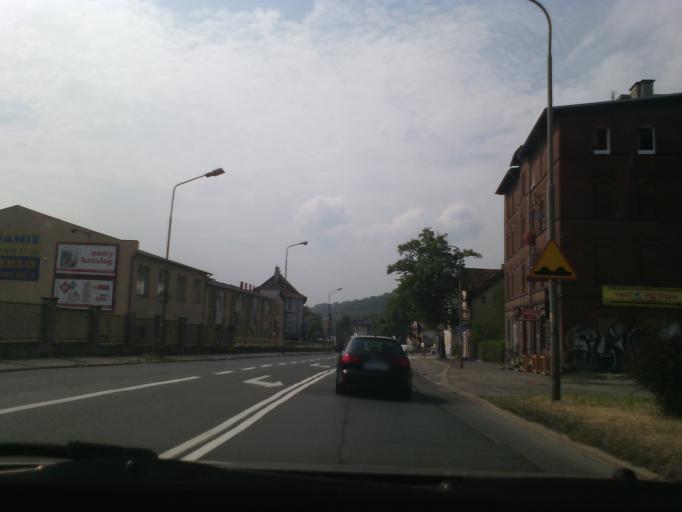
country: PL
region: Lower Silesian Voivodeship
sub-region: Powiat walbrzyski
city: Walbrzych
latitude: 50.8023
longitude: 16.2929
